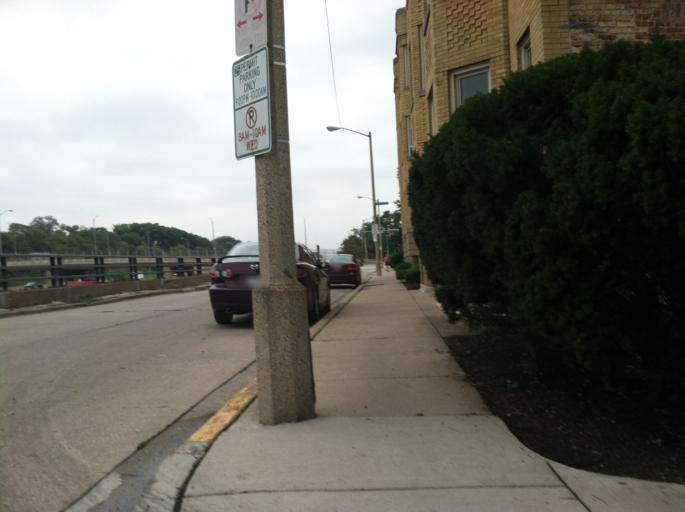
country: US
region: Illinois
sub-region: Cook County
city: Oak Park
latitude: 41.8714
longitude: -87.7860
